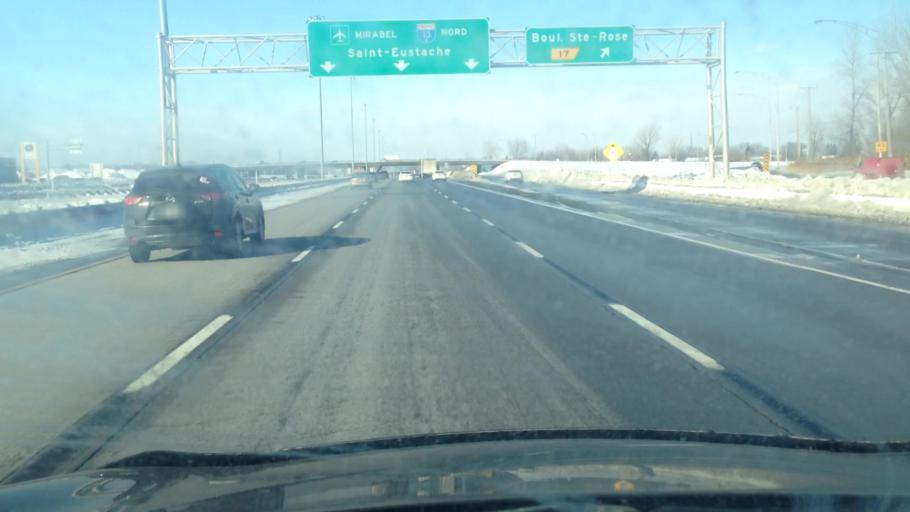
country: CA
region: Quebec
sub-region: Laurentides
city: Boisbriand
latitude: 45.5653
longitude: -73.8205
